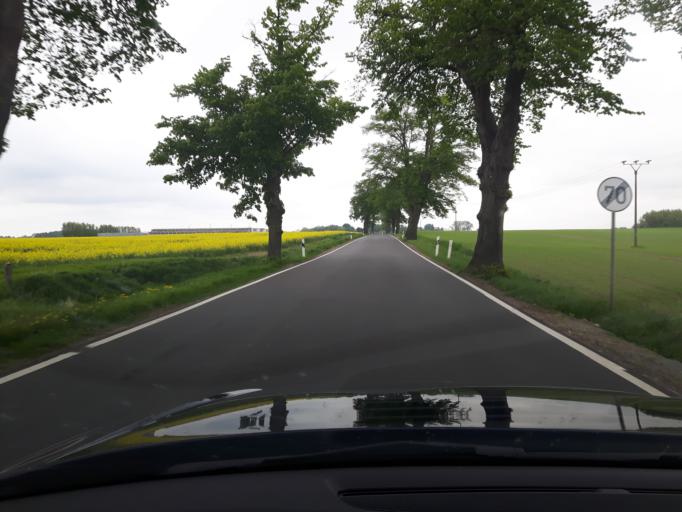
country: DE
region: Mecklenburg-Vorpommern
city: Gnoien
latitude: 54.0194
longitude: 12.6550
